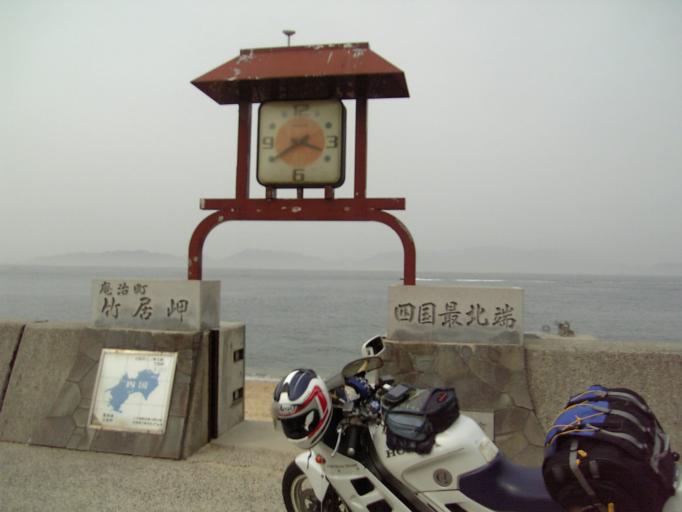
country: JP
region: Kagawa
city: Shido
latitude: 34.3979
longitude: 134.1416
